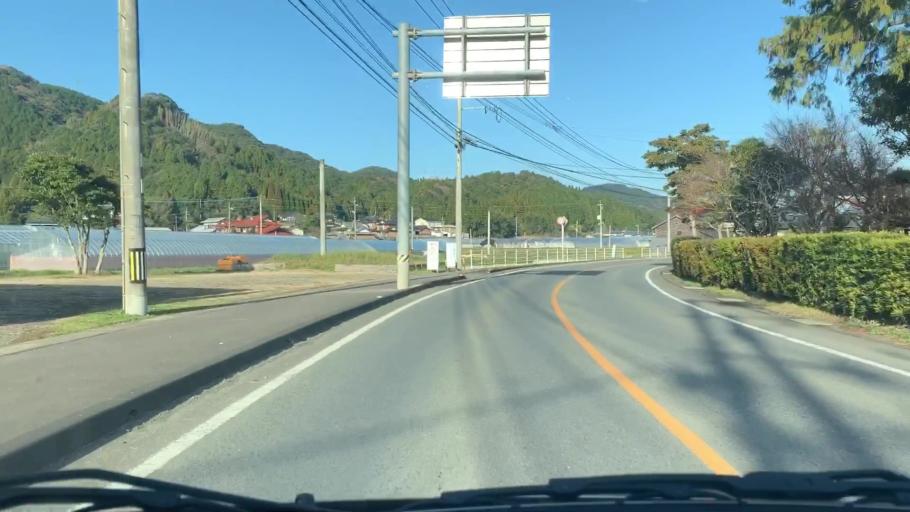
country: JP
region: Saga Prefecture
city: Takeocho-takeo
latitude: 33.2220
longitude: 130.0267
